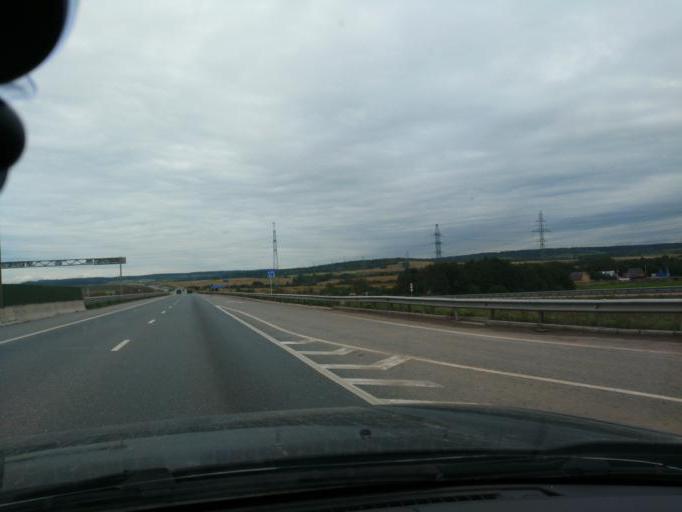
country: RU
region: Perm
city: Ferma
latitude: 57.9306
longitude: 56.3297
